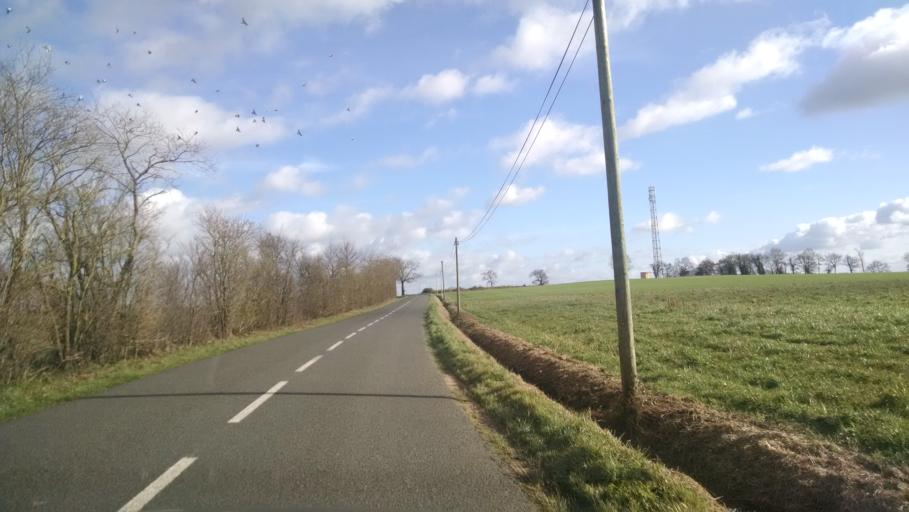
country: FR
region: Pays de la Loire
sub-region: Departement de la Loire-Atlantique
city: Remouille
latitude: 47.0582
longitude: -1.3549
